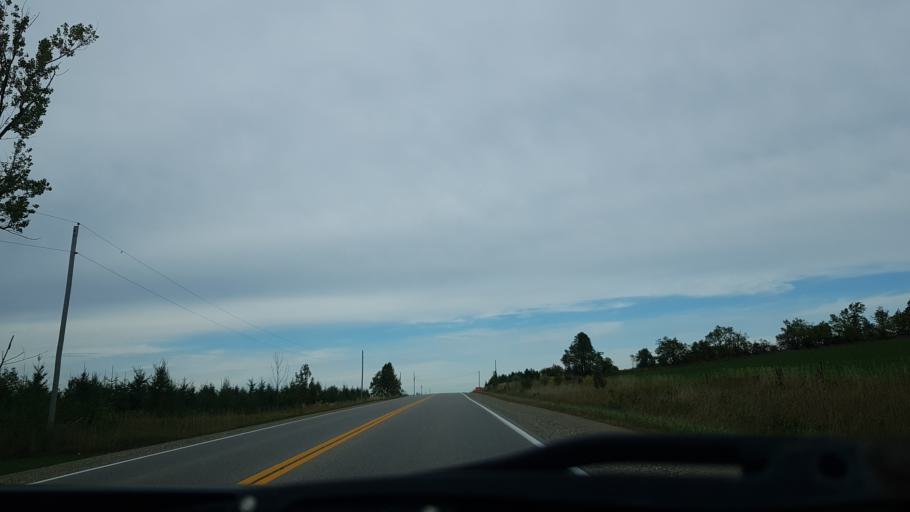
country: CA
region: Ontario
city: Shelburne
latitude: 44.0987
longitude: -80.0230
